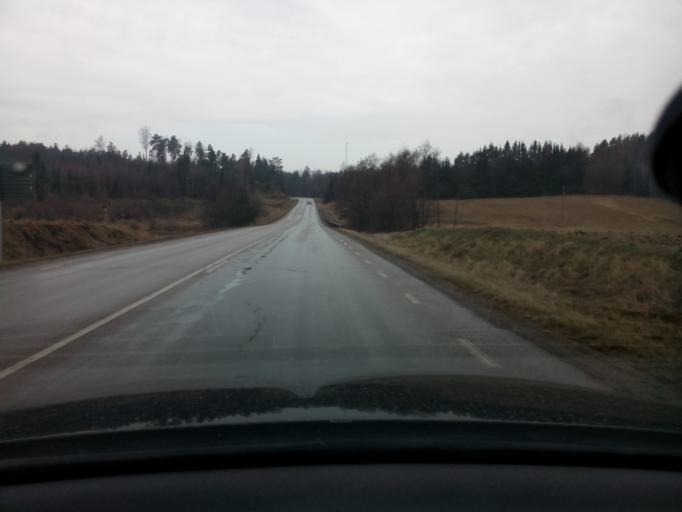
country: SE
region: Soedermanland
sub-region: Trosa Kommun
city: Vagnharad
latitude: 58.9369
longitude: 17.4172
